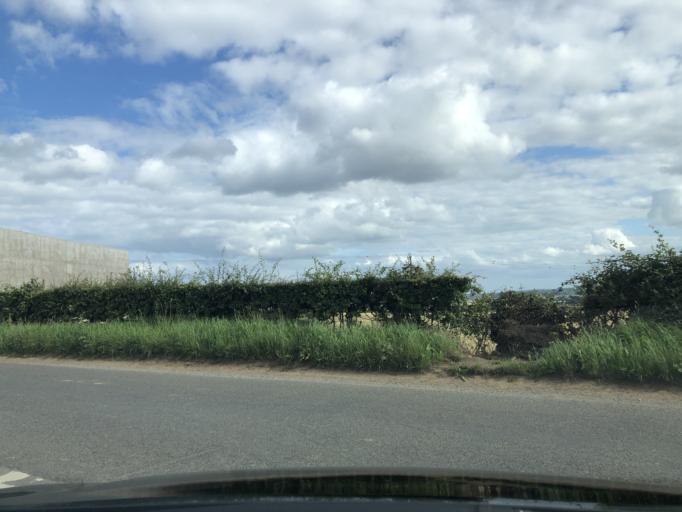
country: GB
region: Northern Ireland
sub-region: Ards District
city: Newtownards
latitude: 54.5726
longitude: -5.7158
